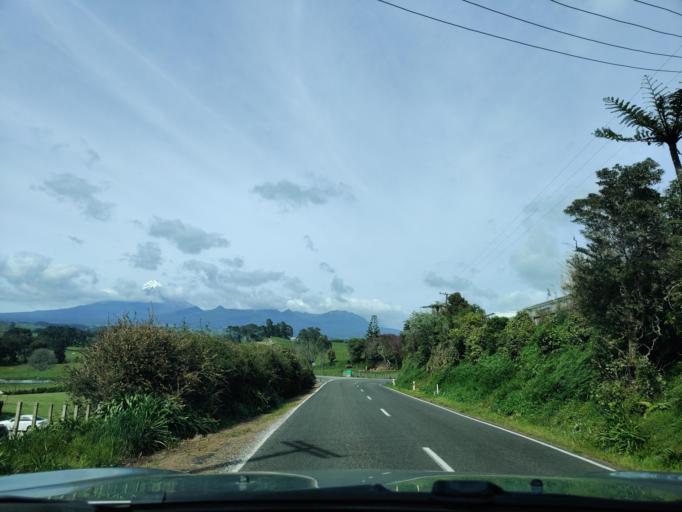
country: NZ
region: Taranaki
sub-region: New Plymouth District
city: New Plymouth
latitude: -39.1178
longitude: 174.0941
